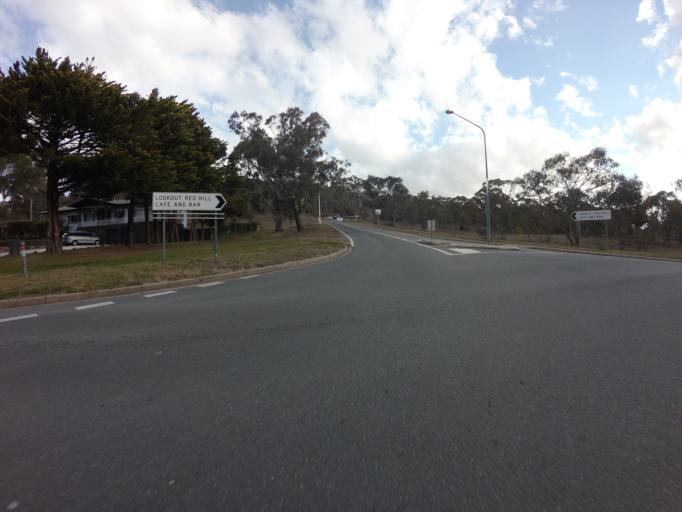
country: AU
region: Australian Capital Territory
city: Forrest
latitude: -35.3196
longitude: 149.1143
